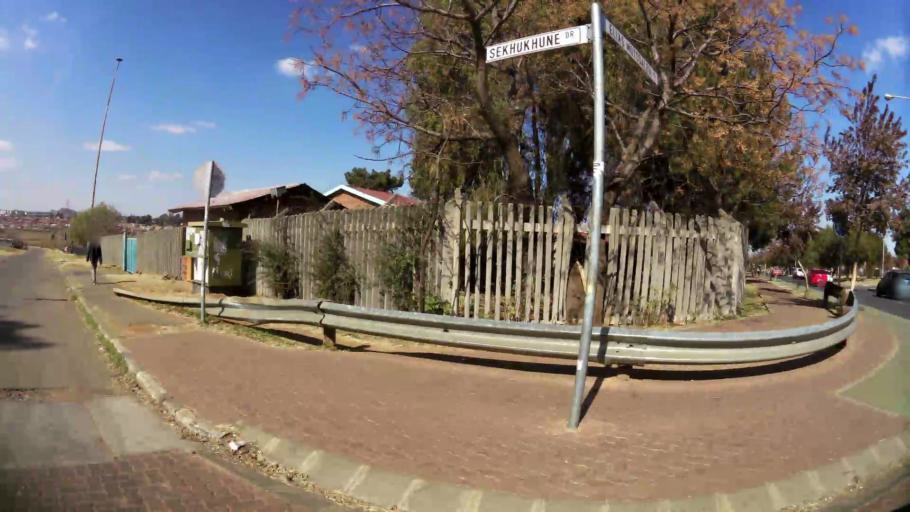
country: ZA
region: Gauteng
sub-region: City of Johannesburg Metropolitan Municipality
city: Soweto
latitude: -26.2576
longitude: 27.8859
